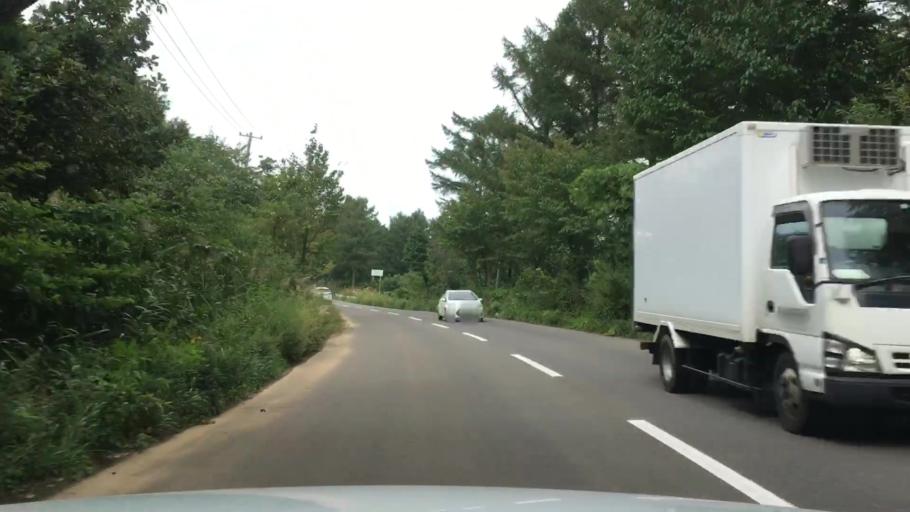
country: JP
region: Aomori
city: Shimokizukuri
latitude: 40.7091
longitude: 140.3378
